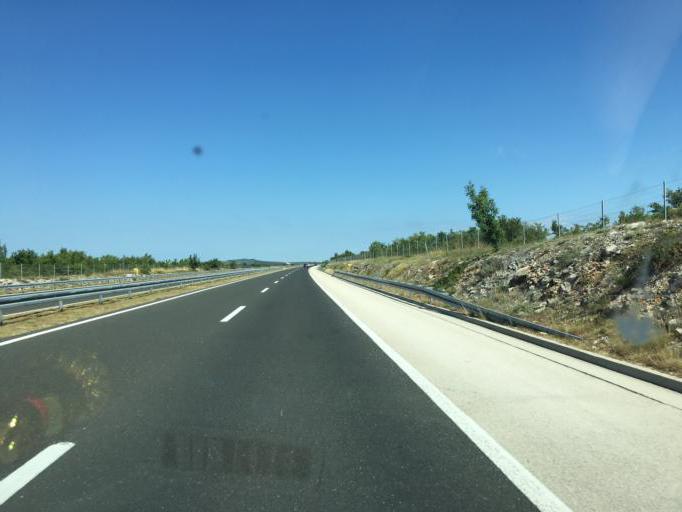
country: HR
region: Zadarska
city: Benkovac
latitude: 44.0192
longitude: 15.5750
